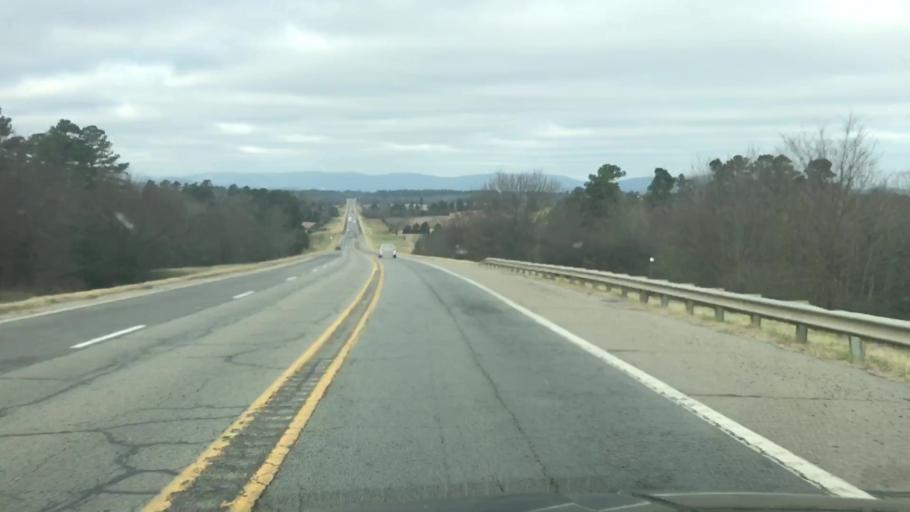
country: US
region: Arkansas
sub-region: Scott County
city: Waldron
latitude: 34.8668
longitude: -94.0765
